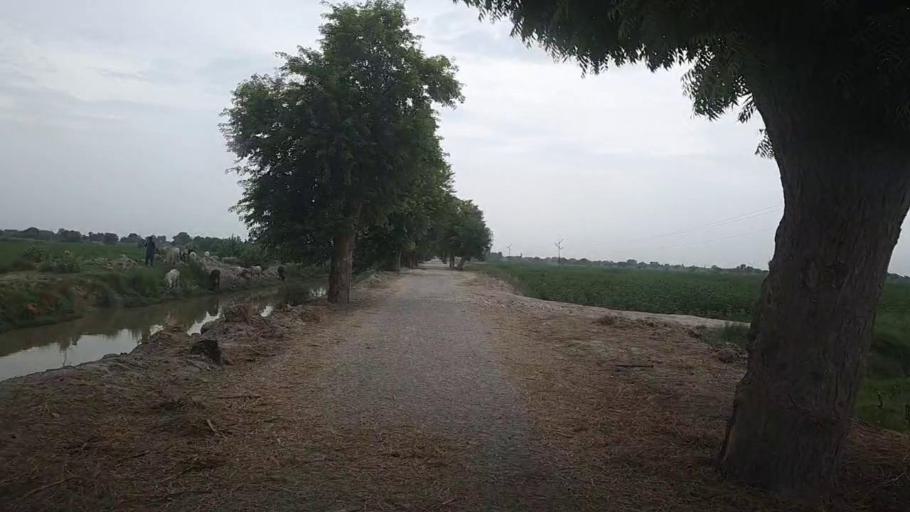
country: PK
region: Sindh
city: Karaundi
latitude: 26.9594
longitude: 68.3648
